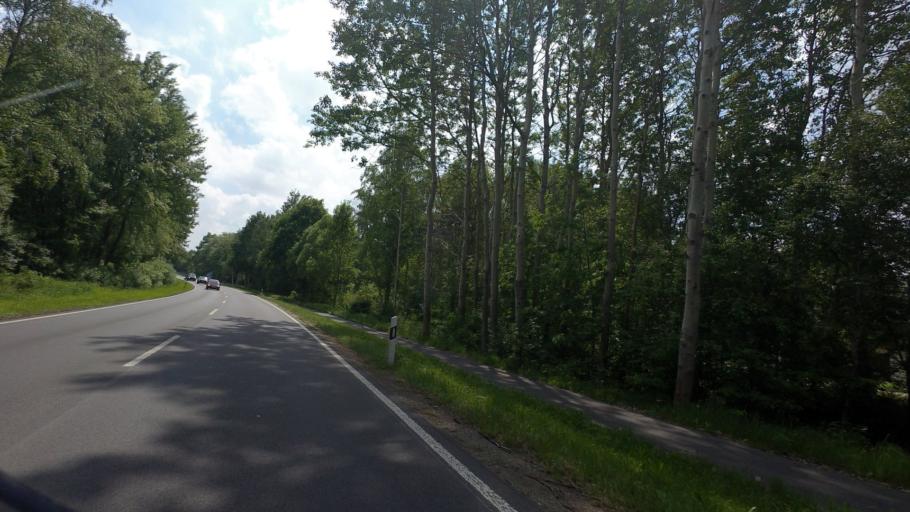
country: DE
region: Saxony
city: Weisswasser
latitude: 51.5206
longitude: 14.6061
